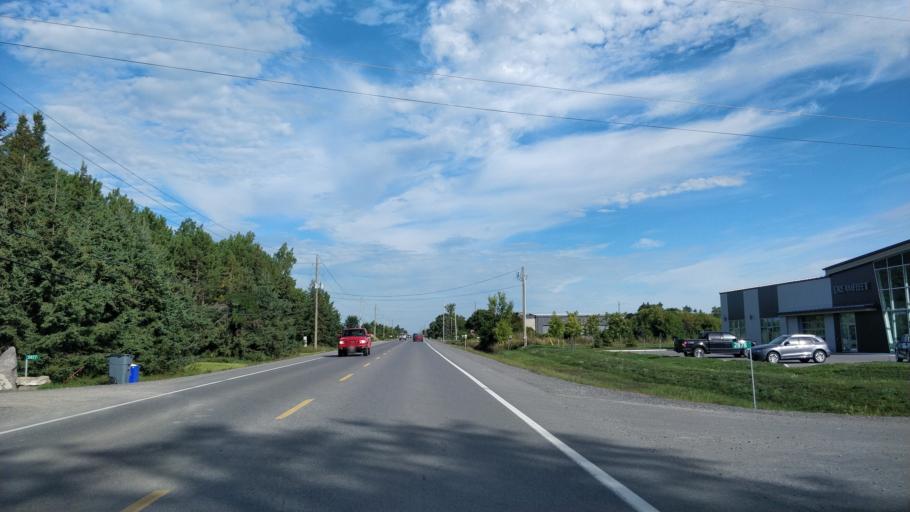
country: CA
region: Ontario
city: Bells Corners
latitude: 45.3084
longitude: -75.9909
